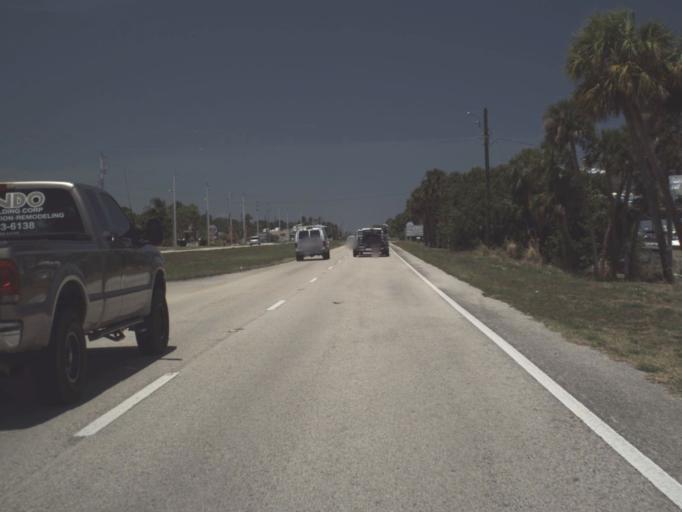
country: US
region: Florida
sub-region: Brevard County
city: Micco
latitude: 27.8713
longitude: -80.4964
